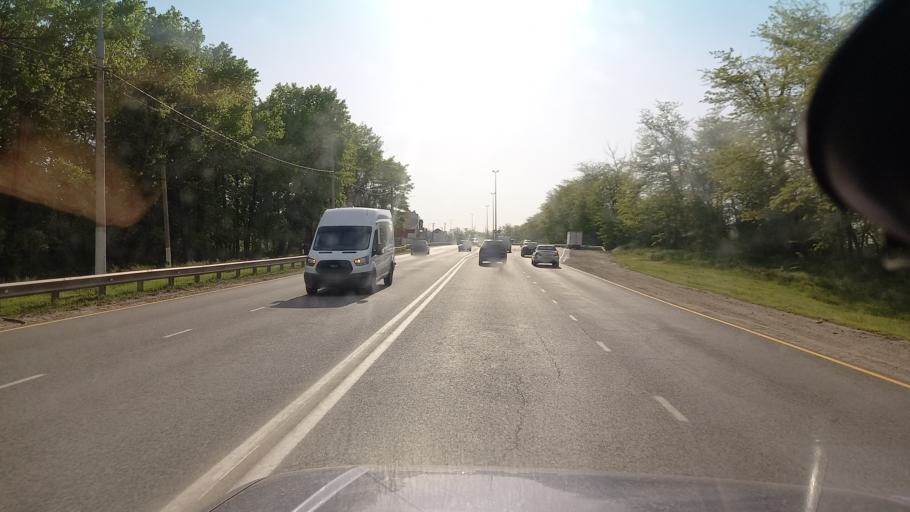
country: RU
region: Krasnodarskiy
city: Yelizavetinskaya
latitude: 45.0567
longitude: 38.8726
